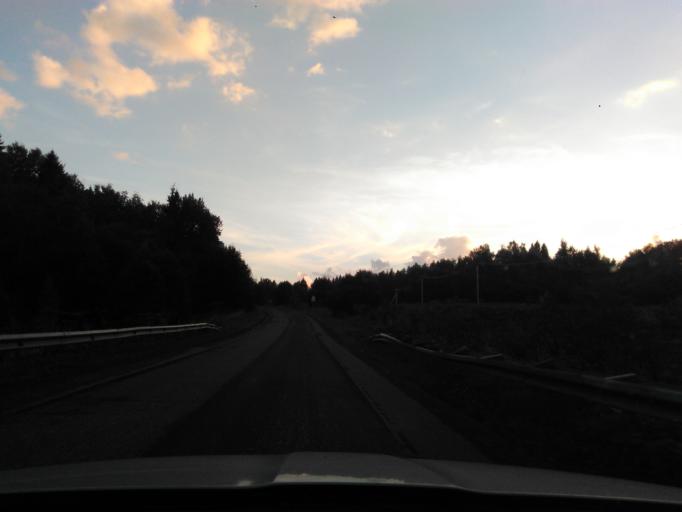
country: RU
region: Moskovskaya
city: Klin
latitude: 56.1808
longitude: 36.7961
